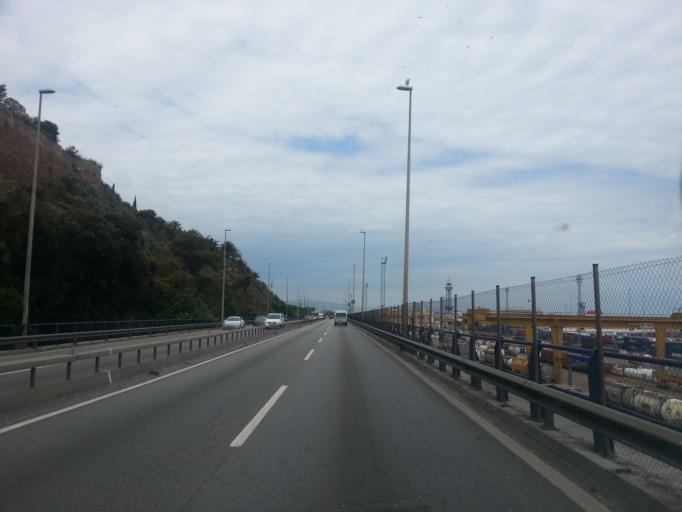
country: ES
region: Catalonia
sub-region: Provincia de Barcelona
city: Sants-Montjuic
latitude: 41.3626
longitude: 2.1695
